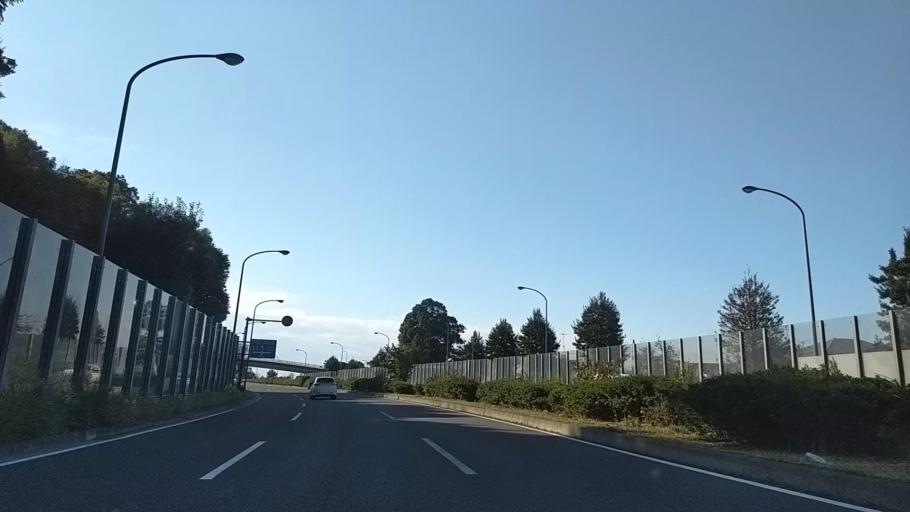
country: JP
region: Kanagawa
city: Yokohama
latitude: 35.4611
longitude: 139.5628
